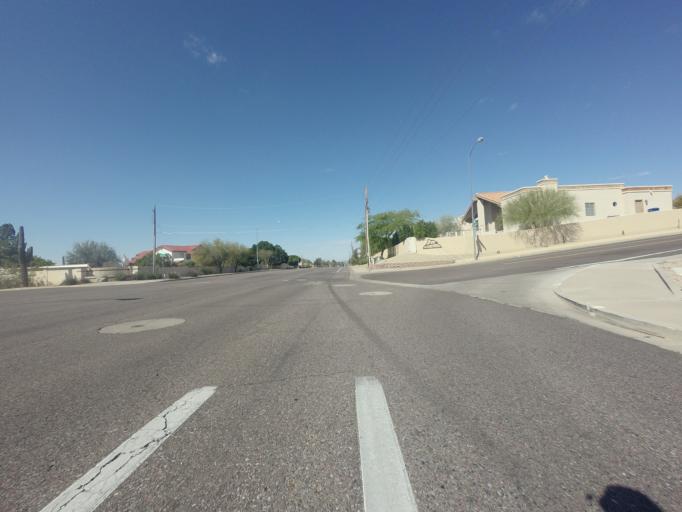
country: US
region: Arizona
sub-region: Maricopa County
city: Mesa
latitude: 33.4664
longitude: -111.6925
